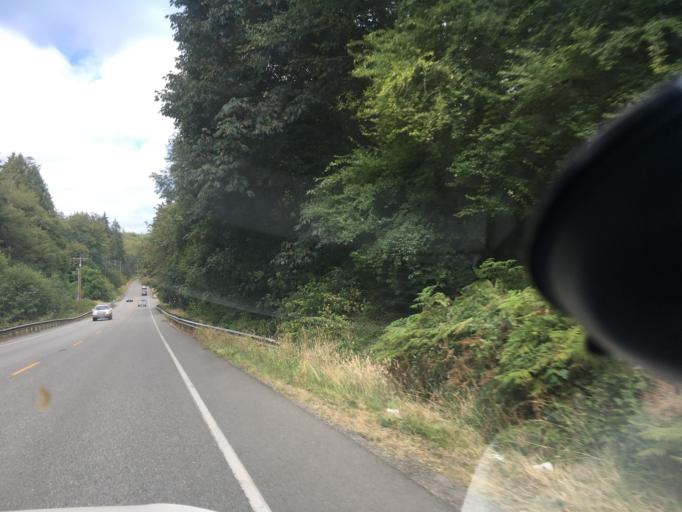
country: US
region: Washington
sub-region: Kitsap County
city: Lofall
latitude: 47.8104
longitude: -122.5788
